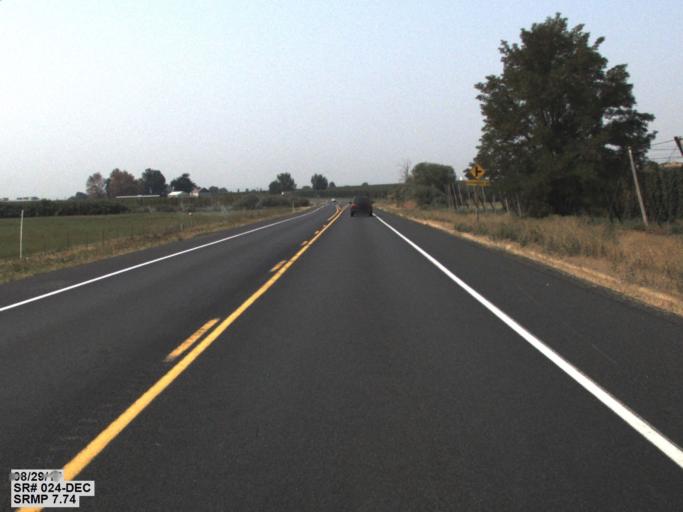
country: US
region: Washington
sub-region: Yakima County
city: Terrace Heights
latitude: 46.5475
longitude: -120.3311
